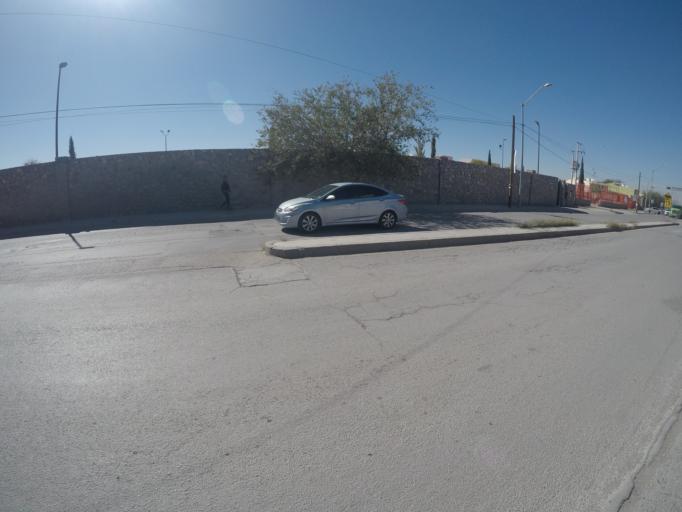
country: US
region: Texas
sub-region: El Paso County
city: Socorro
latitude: 31.6932
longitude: -106.3689
